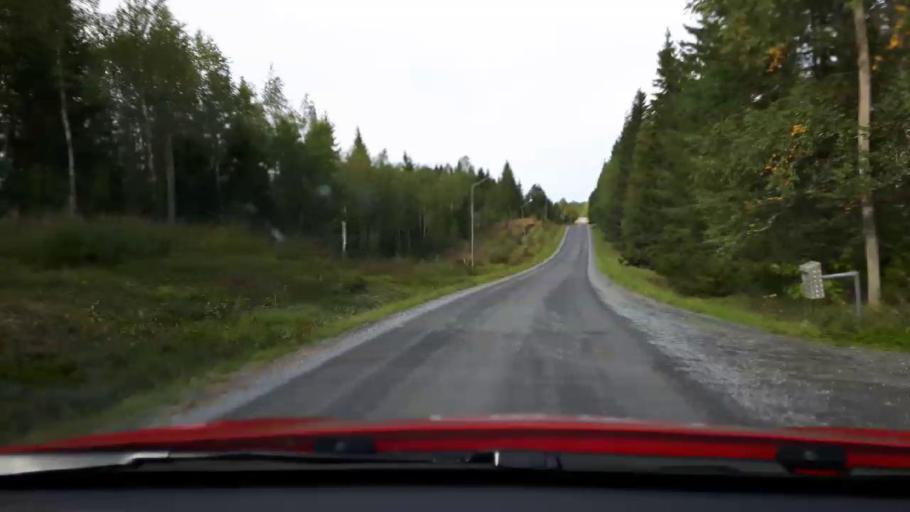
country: SE
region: Jaemtland
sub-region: Krokoms Kommun
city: Valla
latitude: 63.2598
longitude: 13.9261
